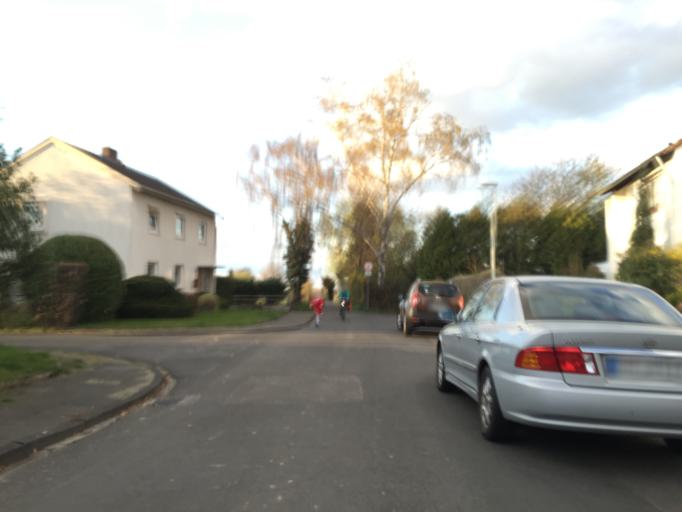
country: DE
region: North Rhine-Westphalia
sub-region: Regierungsbezirk Koln
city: Alfter
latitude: 50.7223
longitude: 7.0541
